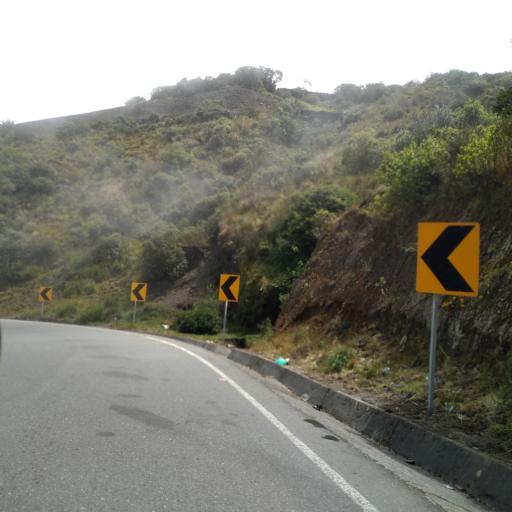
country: EC
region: Cotopaxi
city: La Mana
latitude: -0.9877
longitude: -78.9651
